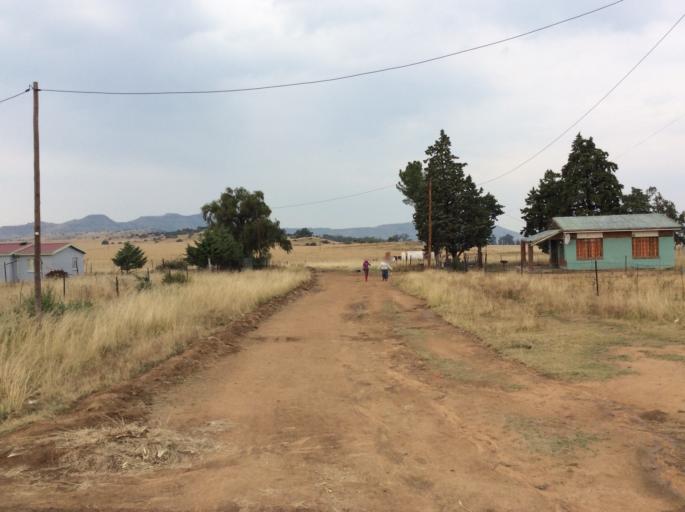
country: LS
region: Mafeteng
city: Mafeteng
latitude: -29.9904
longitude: 27.0155
